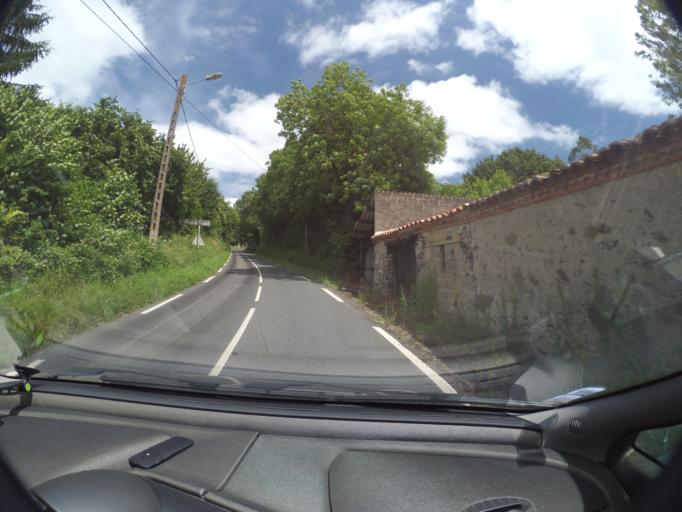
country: FR
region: Pays de la Loire
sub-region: Departement de la Loire-Atlantique
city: Gorges
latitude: 47.1079
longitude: -1.3034
